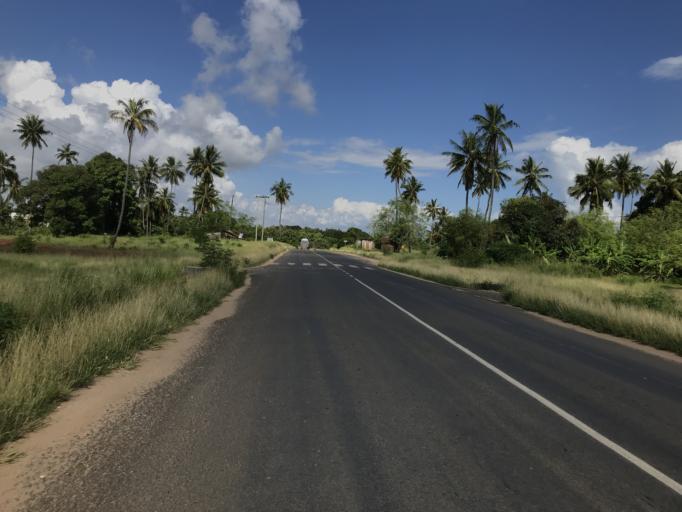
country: TZ
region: Dar es Salaam
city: Dar es Salaam
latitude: -6.8881
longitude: 39.4217
